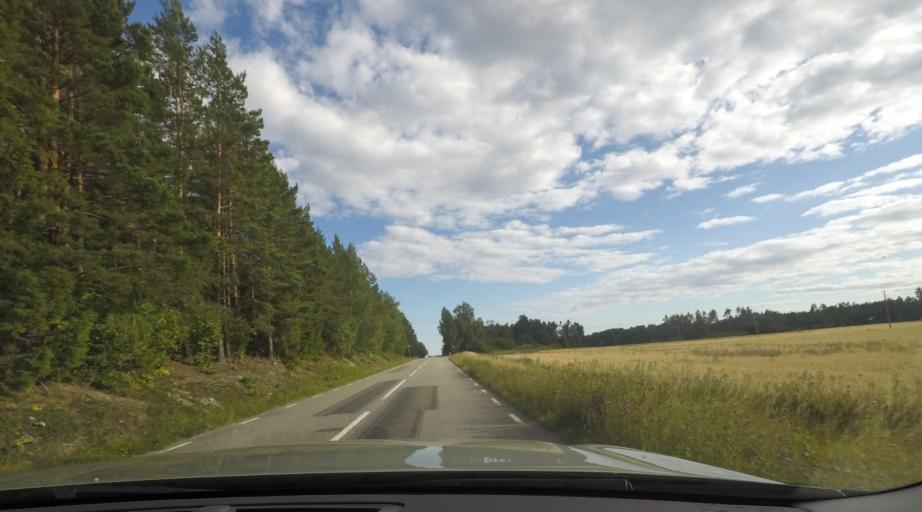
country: SE
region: Soedermanland
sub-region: Trosa Kommun
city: Trosa
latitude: 58.9776
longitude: 17.6926
